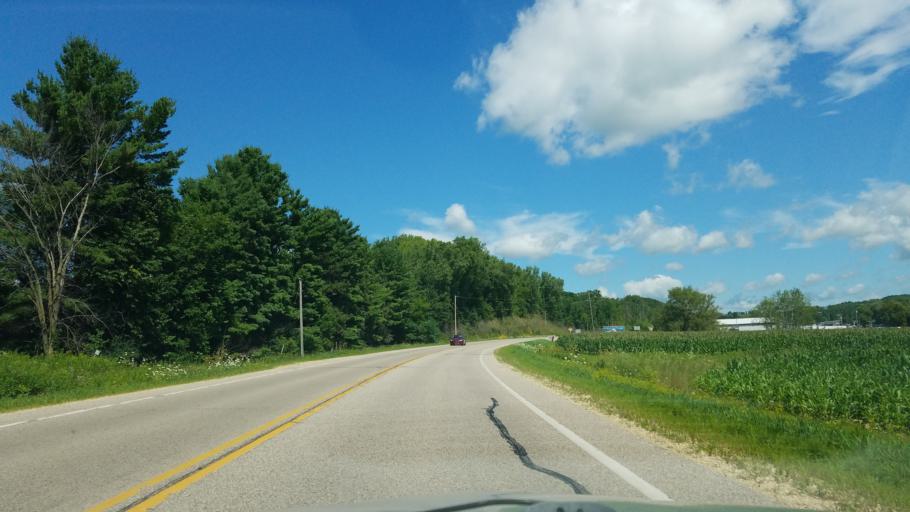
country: US
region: Wisconsin
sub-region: Saint Croix County
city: Glenwood City
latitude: 45.0501
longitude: -92.1767
